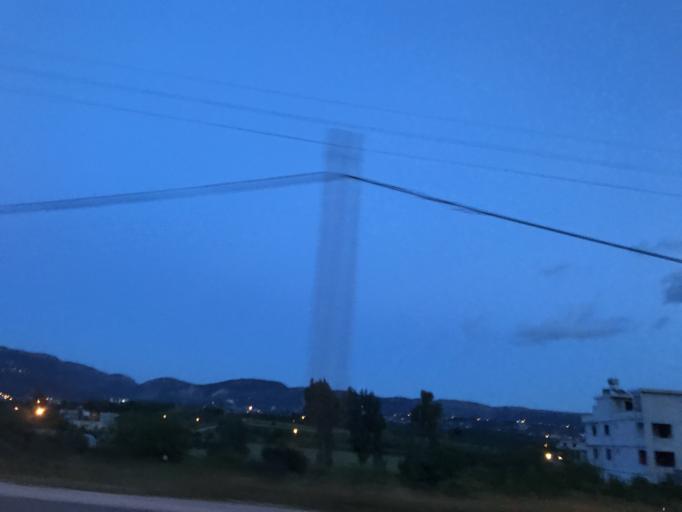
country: TR
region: Hatay
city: Samankaya
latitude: 36.1686
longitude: 36.1078
